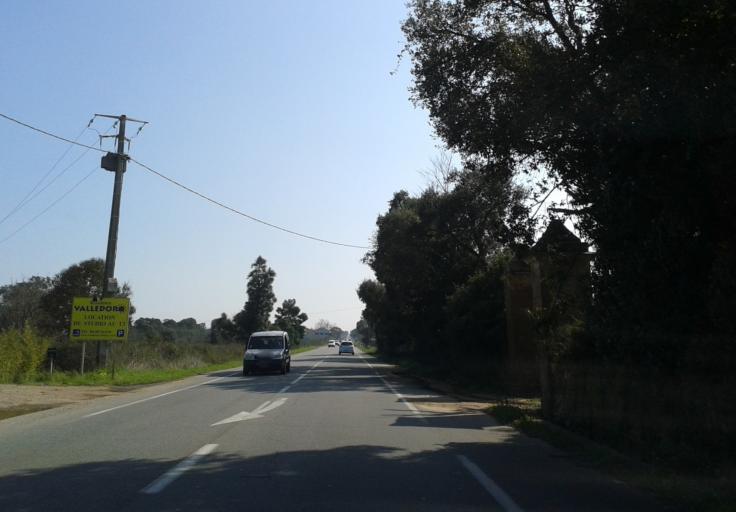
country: FR
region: Corsica
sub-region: Departement de la Haute-Corse
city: San-Nicolao
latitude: 42.3381
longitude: 9.5355
